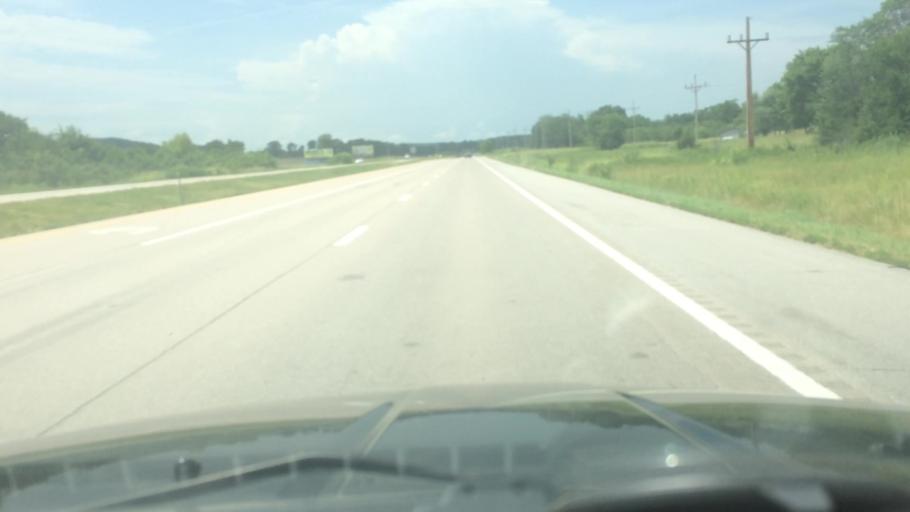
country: US
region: Missouri
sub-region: Polk County
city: Humansville
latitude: 37.8128
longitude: -93.6067
